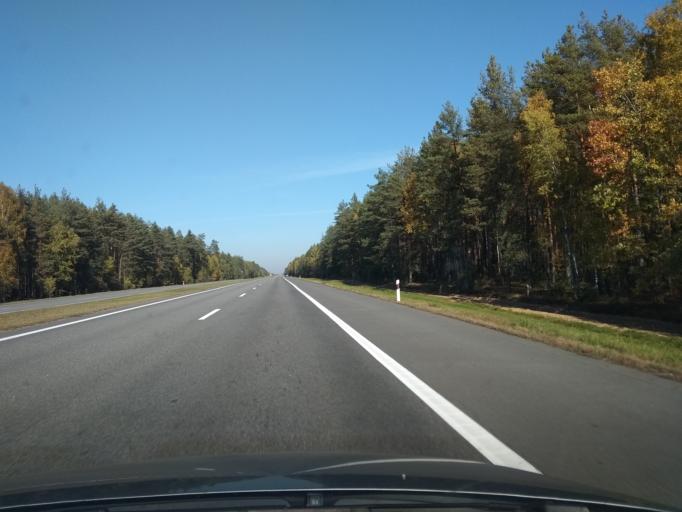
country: BY
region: Grodnenskaya
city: Zhyrovichy
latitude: 52.8820
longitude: 25.6644
